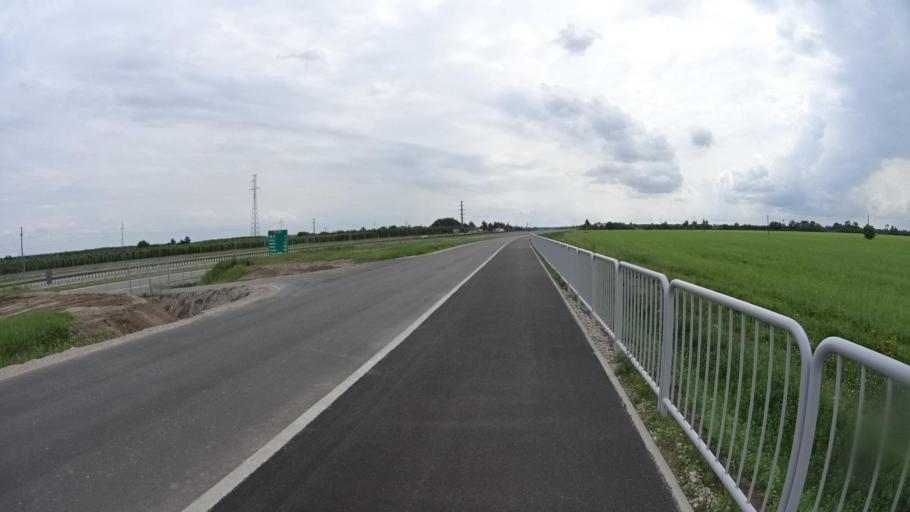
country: PL
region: Masovian Voivodeship
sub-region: Powiat piaseczynski
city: Tarczyn
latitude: 51.9390
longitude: 20.8461
